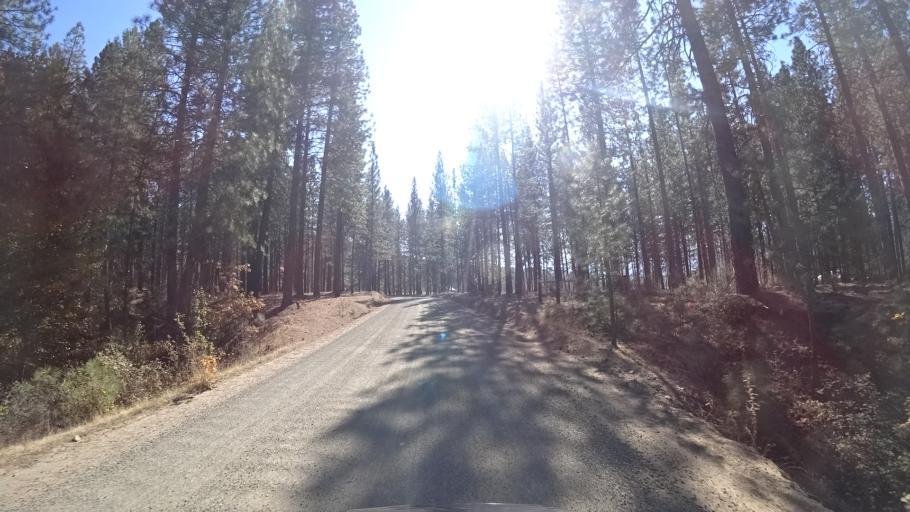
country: US
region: California
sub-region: Siskiyou County
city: Yreka
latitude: 41.5909
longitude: -122.9580
